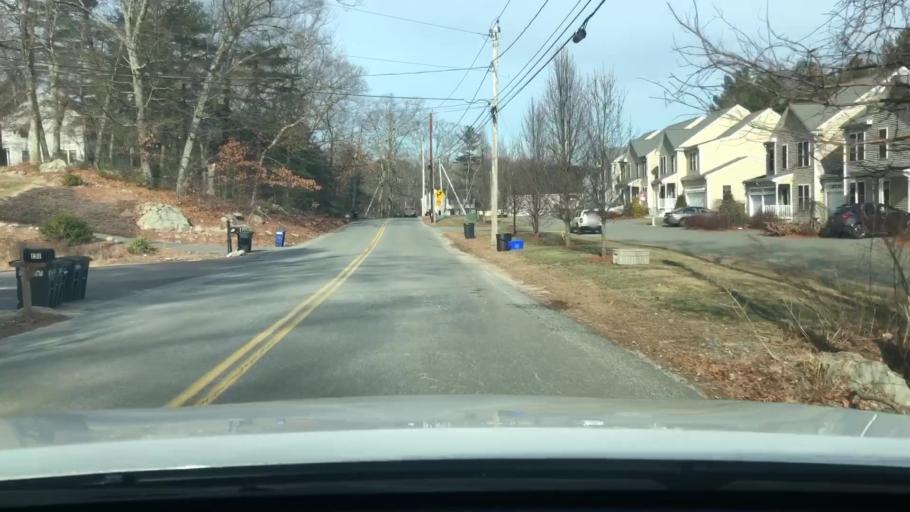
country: US
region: Massachusetts
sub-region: Worcester County
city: Milford
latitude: 42.1218
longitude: -71.4957
